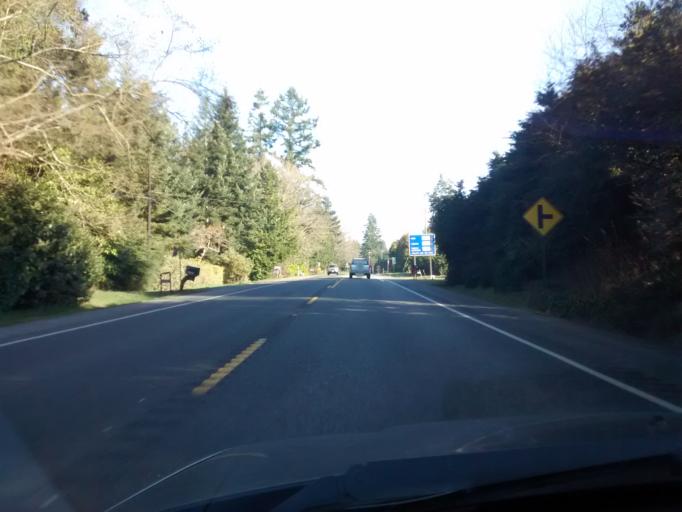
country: US
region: Washington
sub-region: Kitsap County
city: Lofall
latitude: 47.8475
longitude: -122.6141
